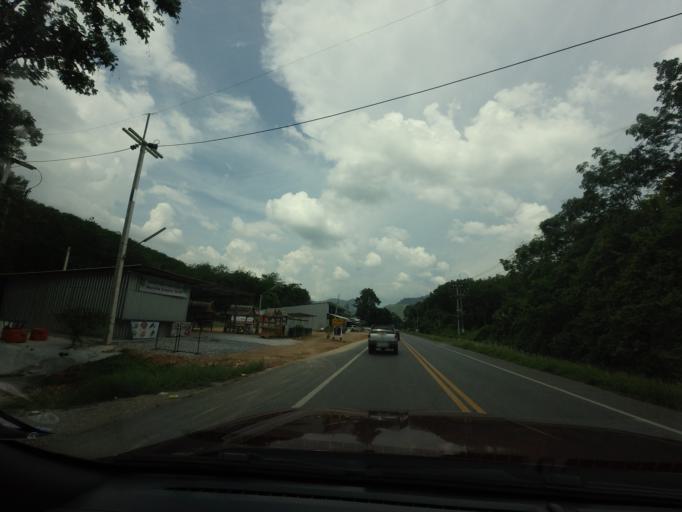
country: TH
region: Yala
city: Ban Nang Sata
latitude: 6.2647
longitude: 101.2731
